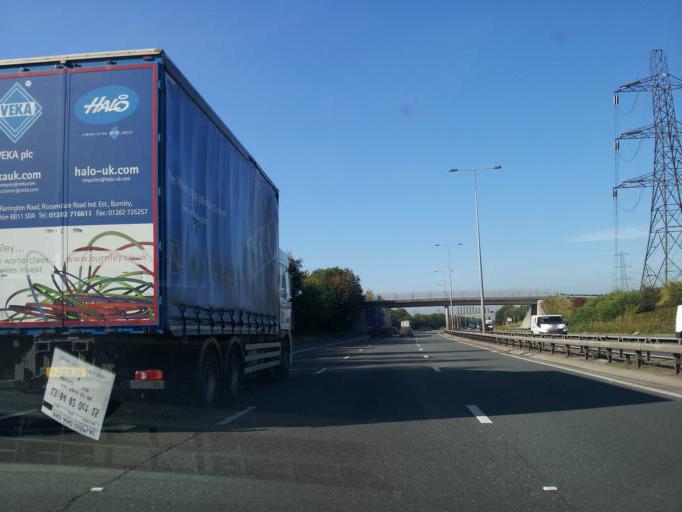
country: GB
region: England
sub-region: Manchester
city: Failsworth
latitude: 53.5280
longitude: -2.1820
